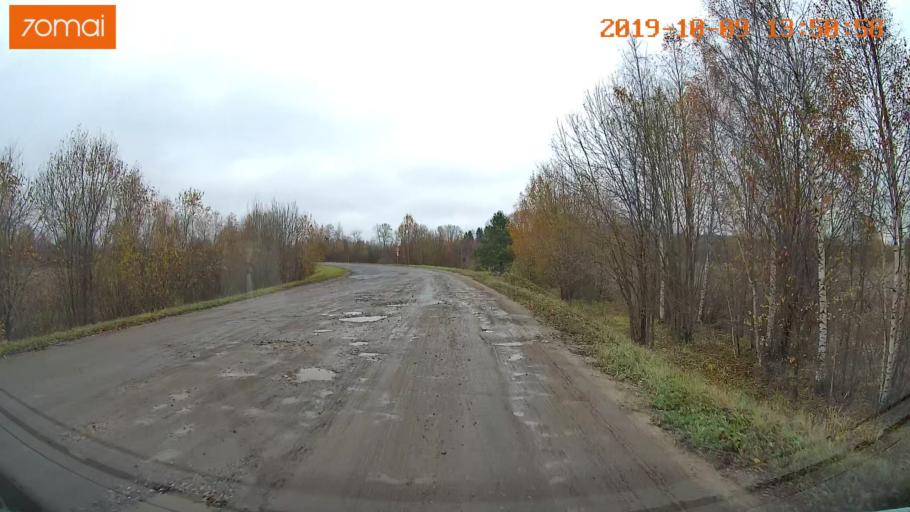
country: RU
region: Kostroma
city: Buy
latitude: 58.4054
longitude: 41.2416
